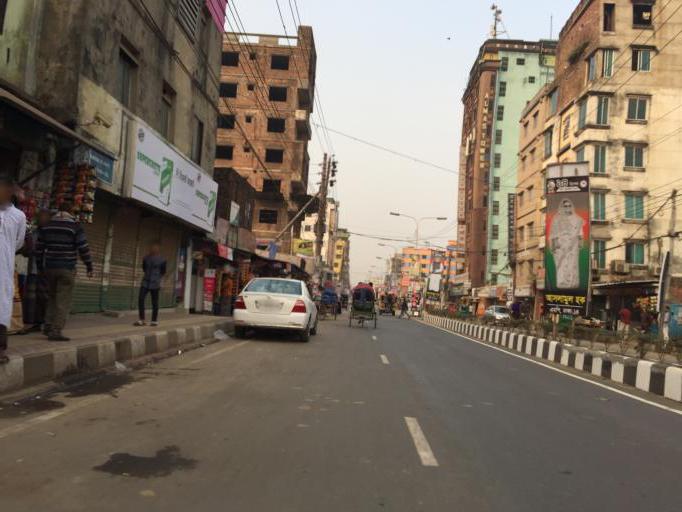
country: BD
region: Dhaka
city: Azimpur
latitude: 23.7860
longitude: 90.3476
